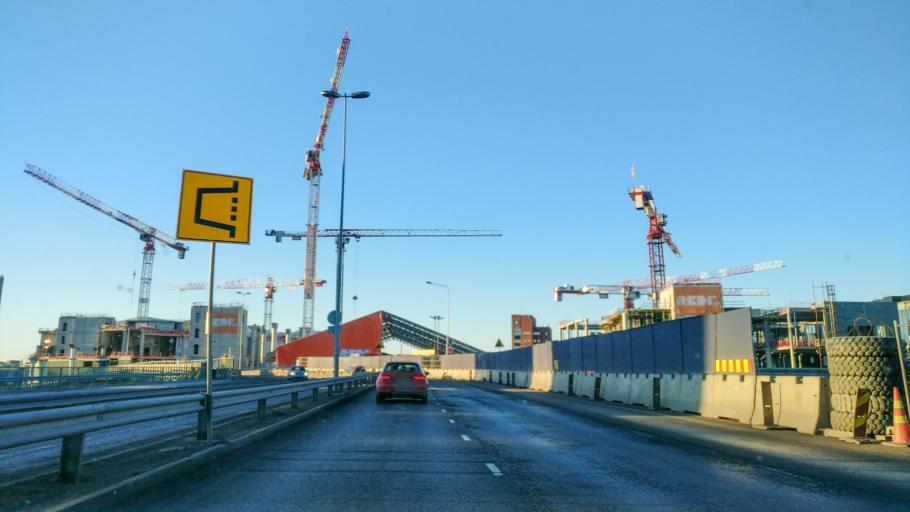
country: FI
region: Uusimaa
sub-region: Helsinki
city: Helsinki
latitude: 60.1866
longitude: 24.9831
